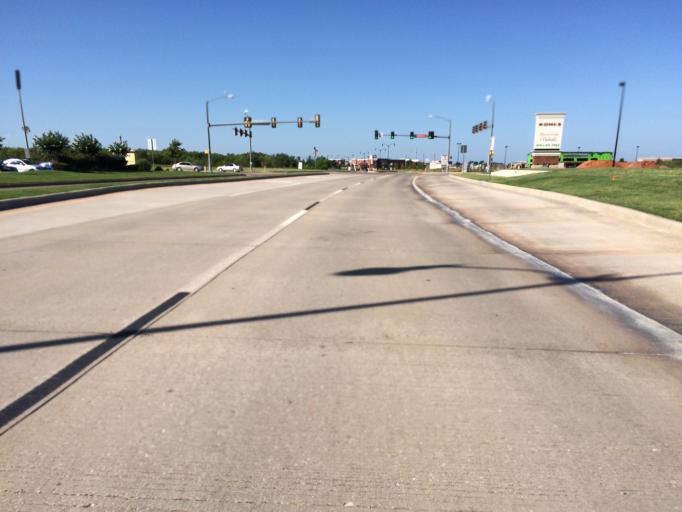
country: US
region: Oklahoma
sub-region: Cleveland County
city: Norman
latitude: 35.2440
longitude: -97.4799
